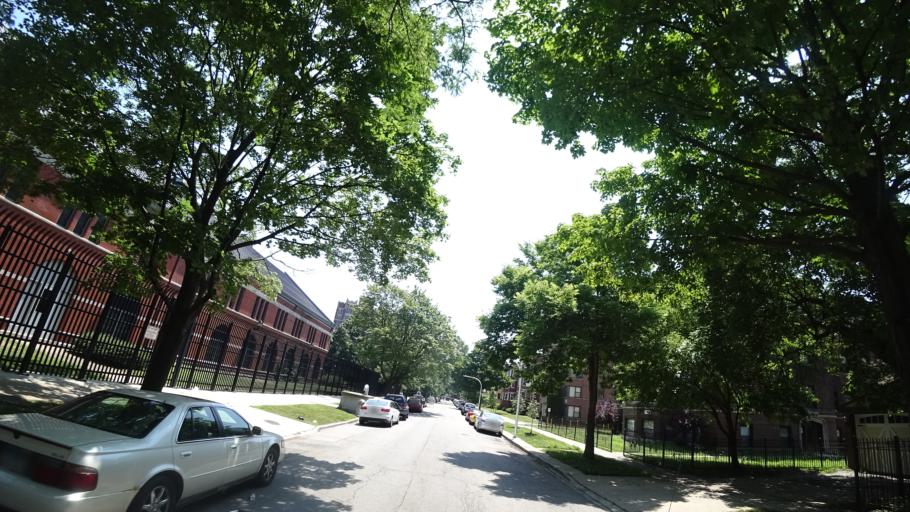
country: US
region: Illinois
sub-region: Cook County
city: Chicago
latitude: 41.7715
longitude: -87.5683
